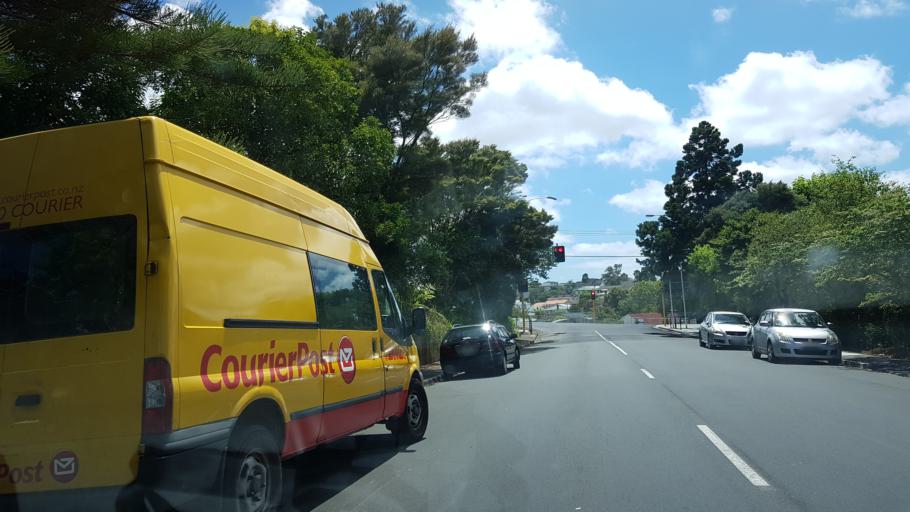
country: NZ
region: Auckland
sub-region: Auckland
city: North Shore
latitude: -36.7750
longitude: 174.7155
